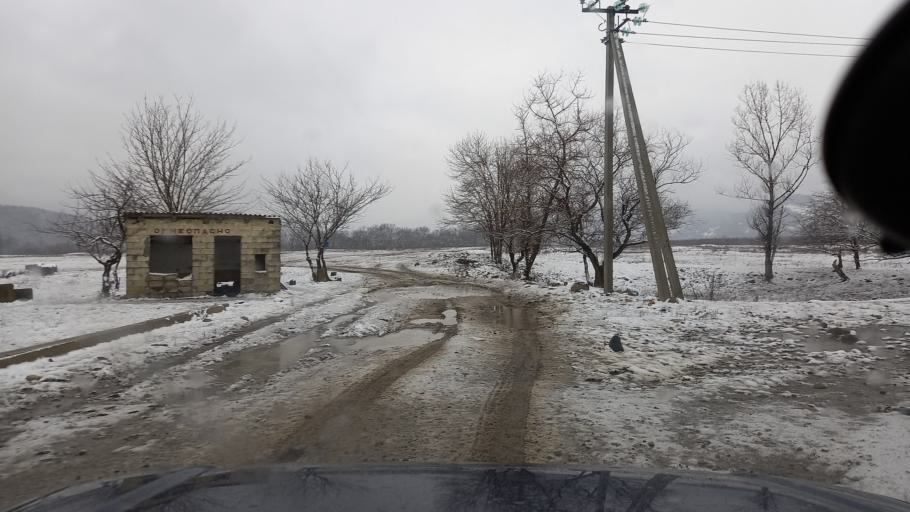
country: RU
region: Adygeya
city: Kamennomostskiy
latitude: 44.2219
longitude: 40.1828
